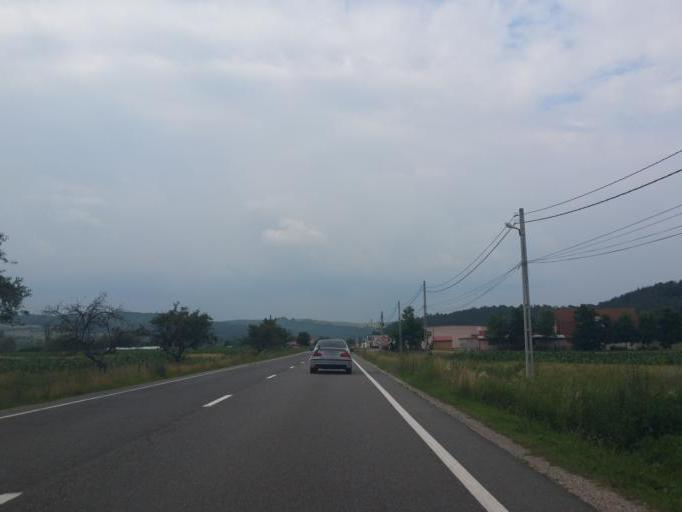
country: RO
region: Salaj
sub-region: Comuna Romanasi
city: Romanasi
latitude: 47.0976
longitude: 23.1881
